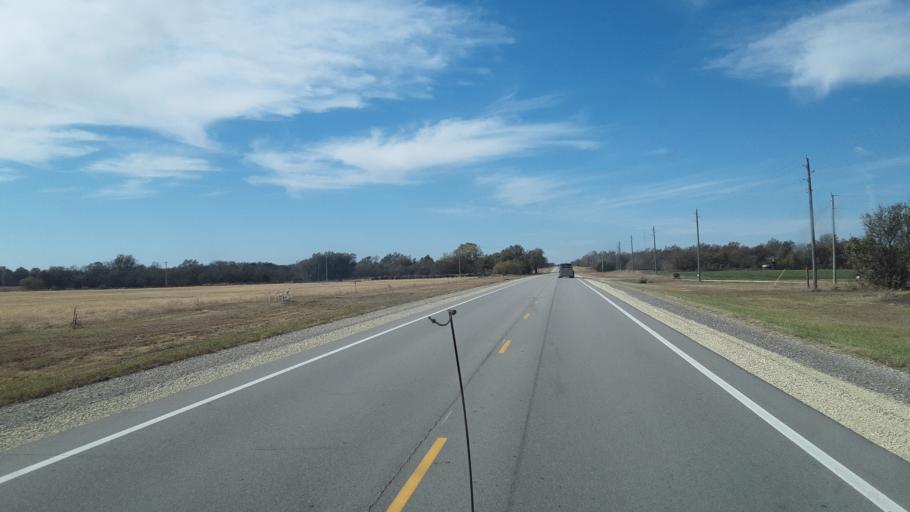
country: US
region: Kansas
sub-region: McPherson County
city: McPherson
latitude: 38.3768
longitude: -97.4902
